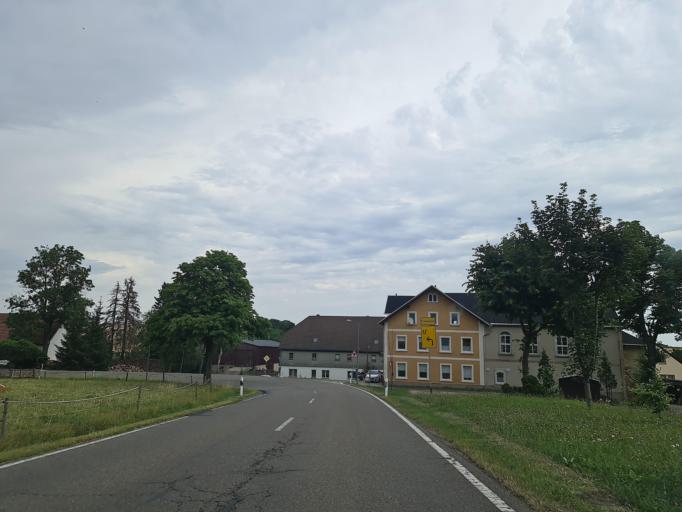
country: DE
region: Saxony
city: Grosshartmannsdorf
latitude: 50.7678
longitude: 13.3380
